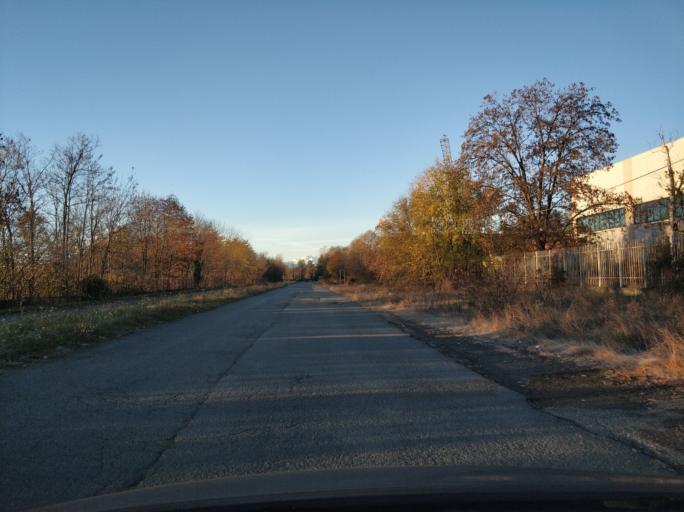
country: IT
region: Piedmont
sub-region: Provincia di Torino
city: Robassomero
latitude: 45.1736
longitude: 7.5958
